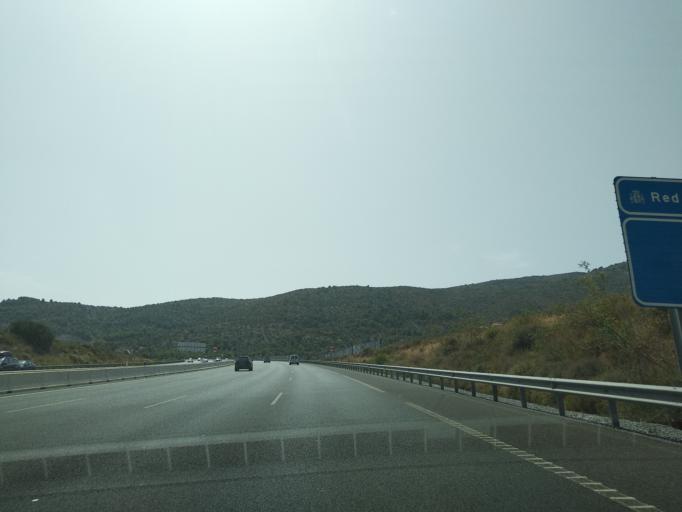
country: ES
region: Andalusia
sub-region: Provincia de Malaga
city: Alhaurin de la Torre
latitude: 36.6651
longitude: -4.5290
